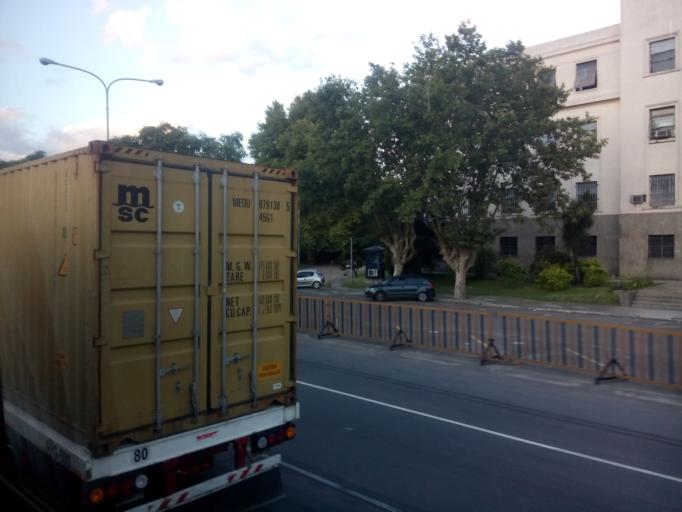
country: AR
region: Buenos Aires F.D.
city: Retiro
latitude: -34.5840
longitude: -58.3730
